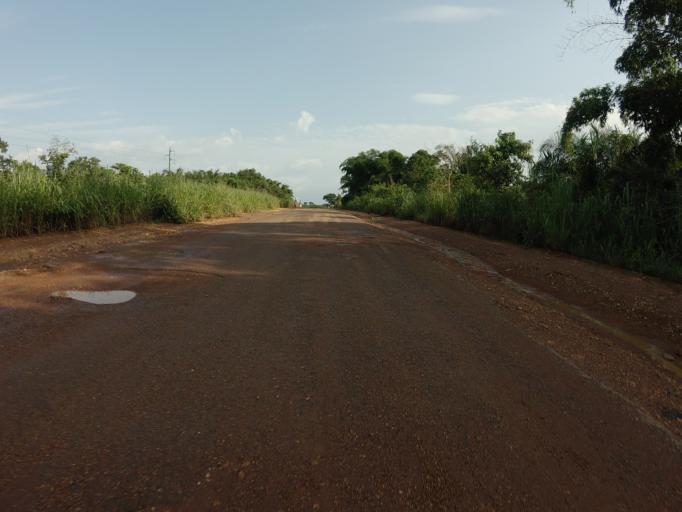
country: GH
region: Volta
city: Hohoe
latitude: 7.0903
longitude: 0.4452
